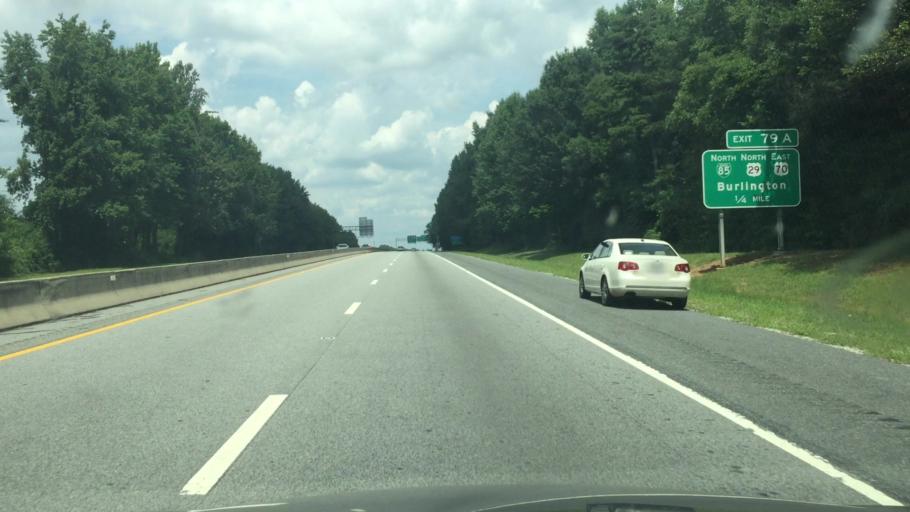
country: US
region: North Carolina
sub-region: Guilford County
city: Greensboro
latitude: 36.0123
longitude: -79.8262
